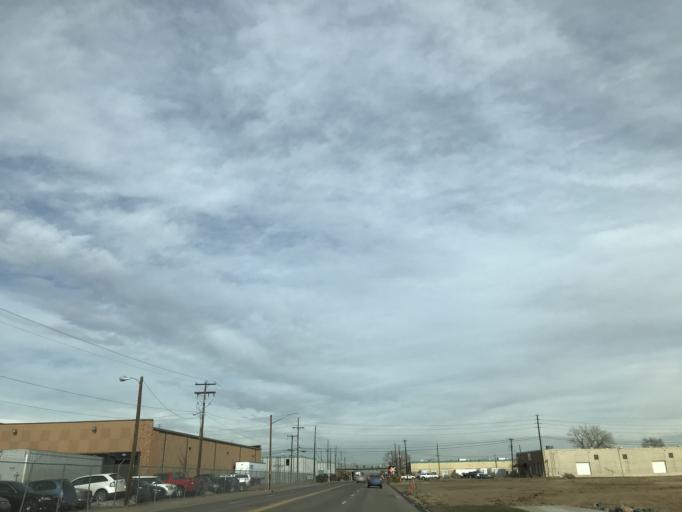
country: US
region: Colorado
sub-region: Adams County
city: Commerce City
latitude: 39.7751
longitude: -104.9128
